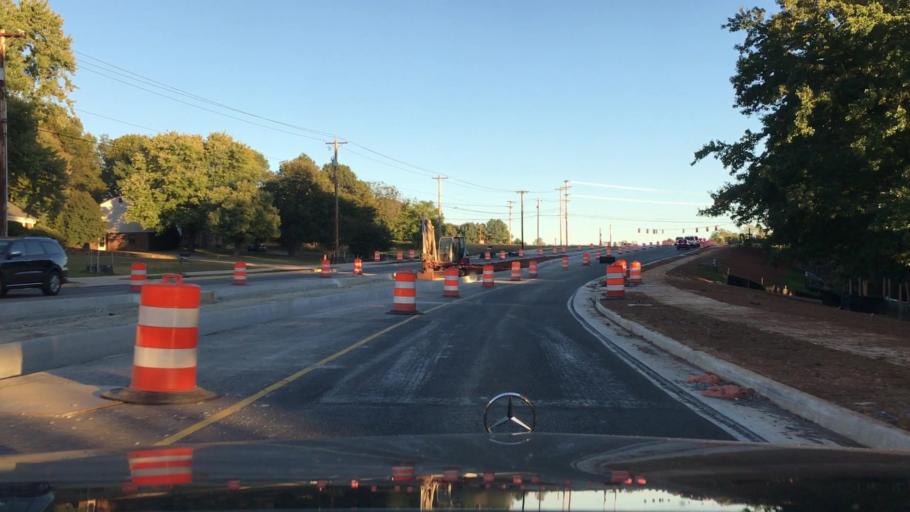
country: US
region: Virginia
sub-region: Campbell County
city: Timberlake
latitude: 37.3354
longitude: -79.2171
